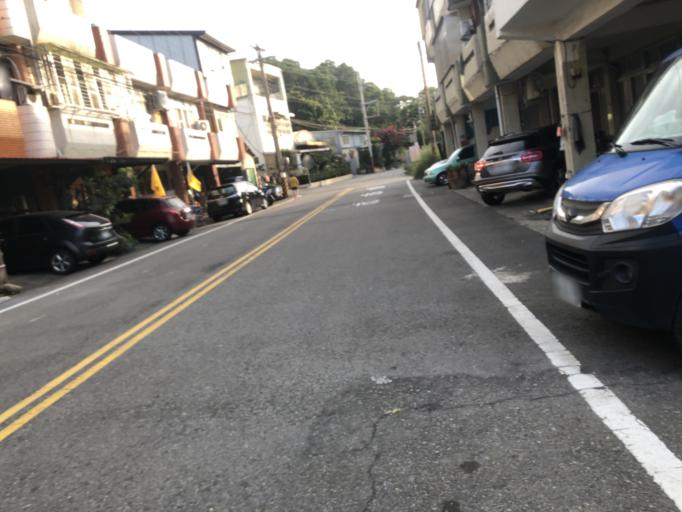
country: TW
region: Taiwan
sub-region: Miaoli
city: Miaoli
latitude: 24.4746
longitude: 120.7959
